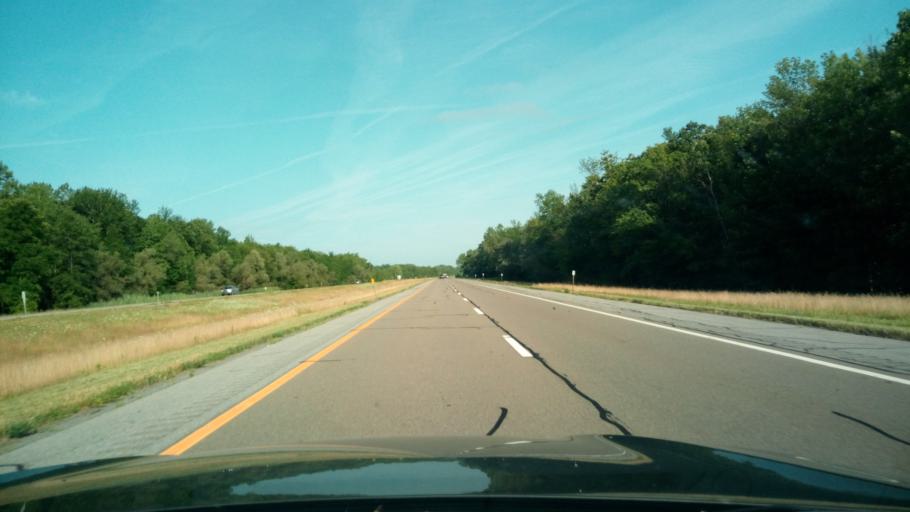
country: US
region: New York
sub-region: Livingston County
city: Mount Morris
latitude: 42.6934
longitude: -77.8086
